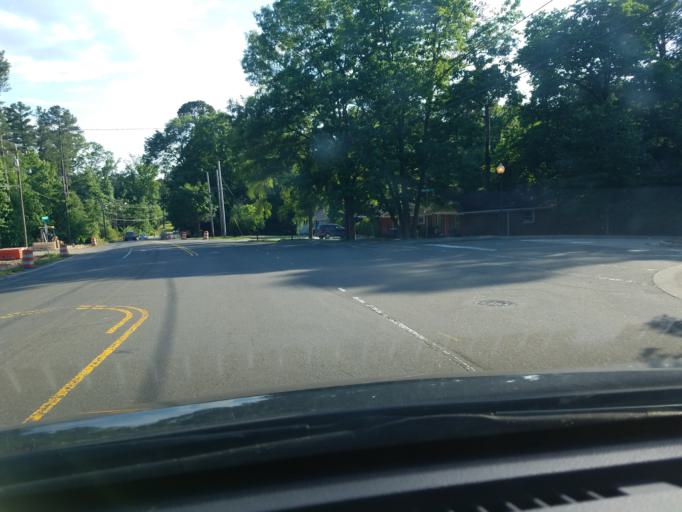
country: US
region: North Carolina
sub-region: Durham County
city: Durham
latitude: 35.9468
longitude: -78.9712
